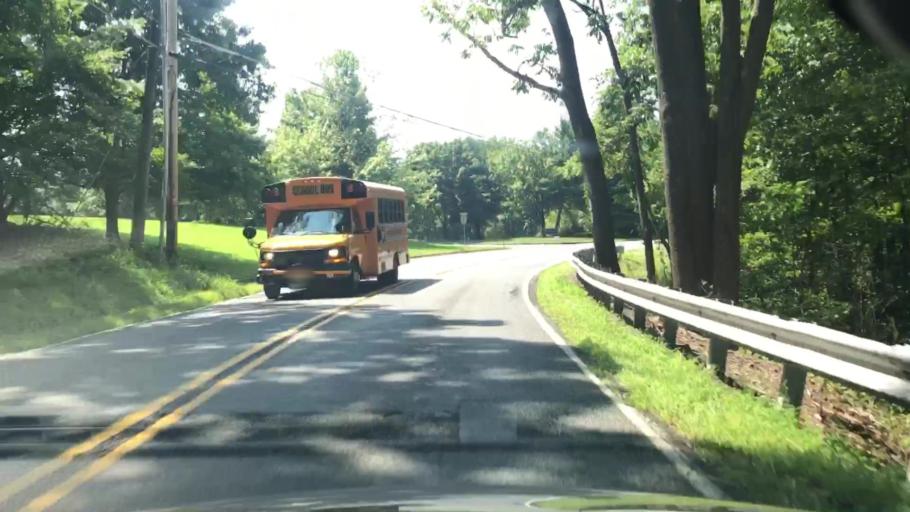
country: US
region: New Jersey
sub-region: Hunterdon County
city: Milford
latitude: 40.6204
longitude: -75.0422
